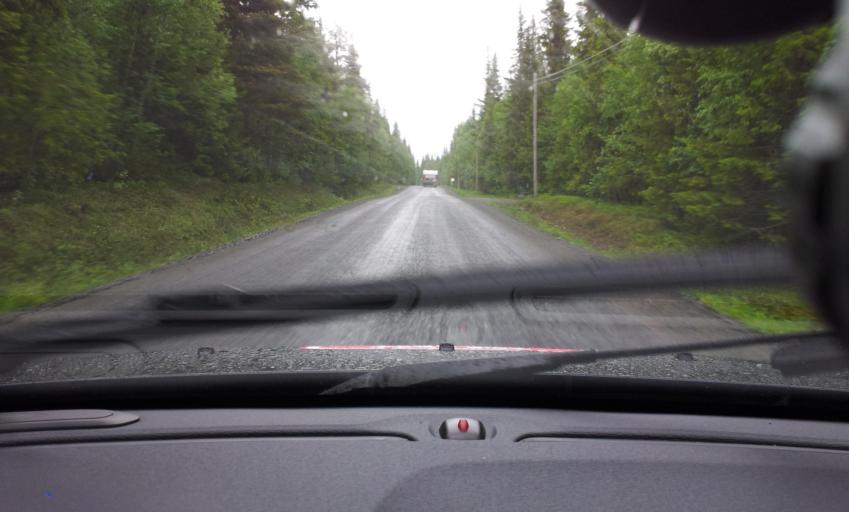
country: SE
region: Jaemtland
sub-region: Are Kommun
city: Are
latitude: 63.1586
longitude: 13.0437
